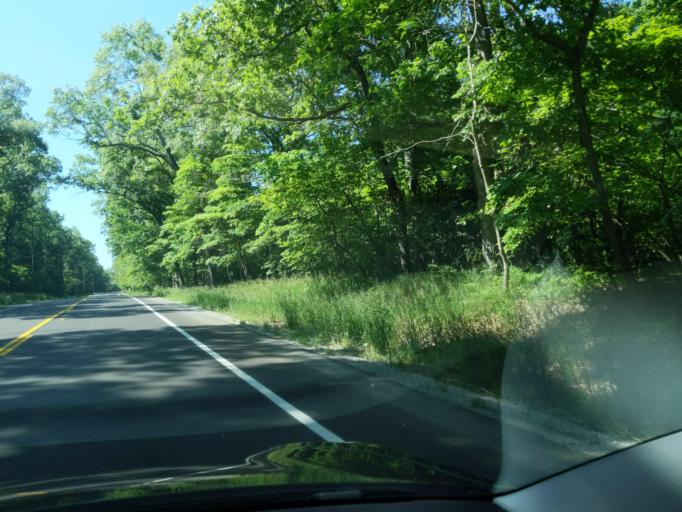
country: US
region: Michigan
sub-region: Muskegon County
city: Montague
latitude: 43.3899
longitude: -86.3962
